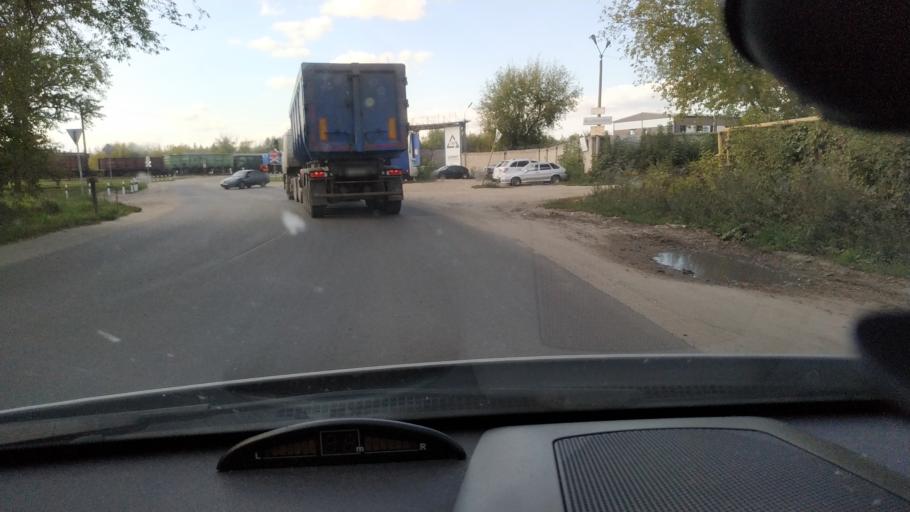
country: RU
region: Rjazan
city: Ryazan'
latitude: 54.6640
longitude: 39.6273
